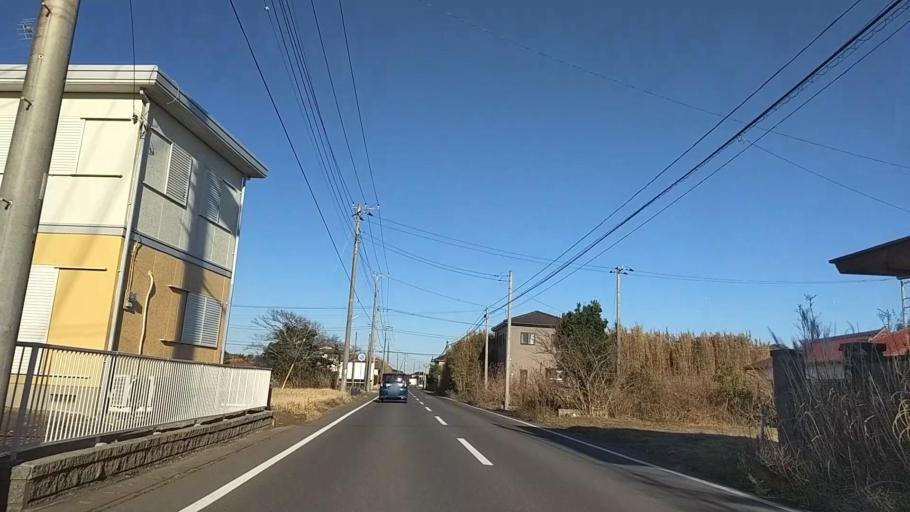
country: JP
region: Chiba
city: Yokaichiba
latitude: 35.6615
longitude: 140.6008
